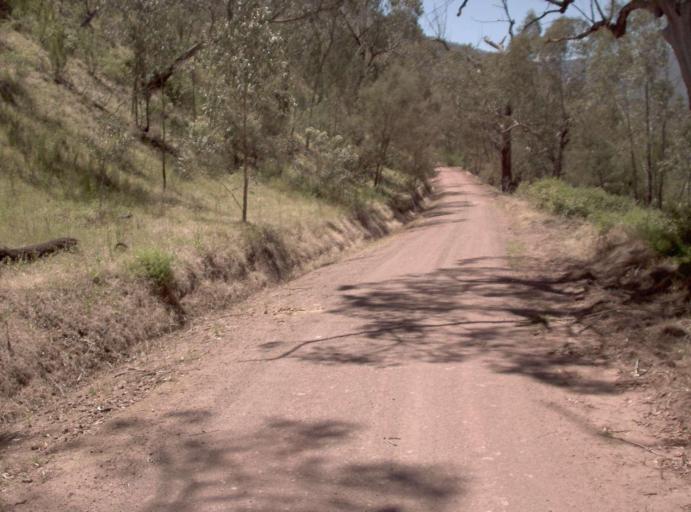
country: AU
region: New South Wales
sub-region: Snowy River
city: Jindabyne
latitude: -36.9186
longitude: 148.4022
